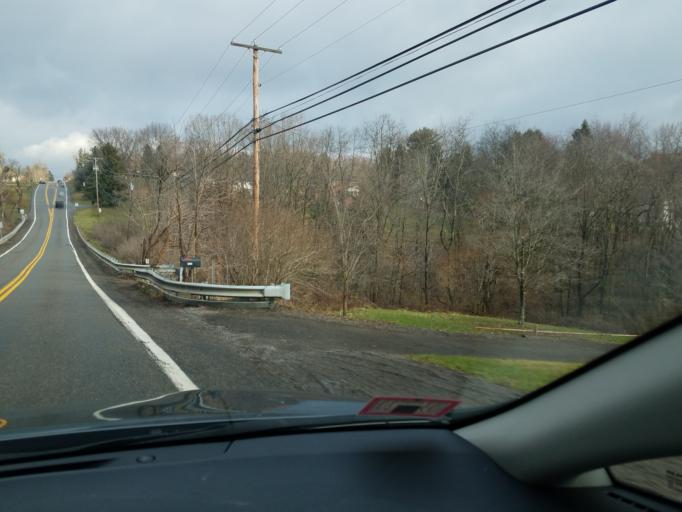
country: US
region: Pennsylvania
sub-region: Allegheny County
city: Franklin Park
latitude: 40.6059
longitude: -80.0995
